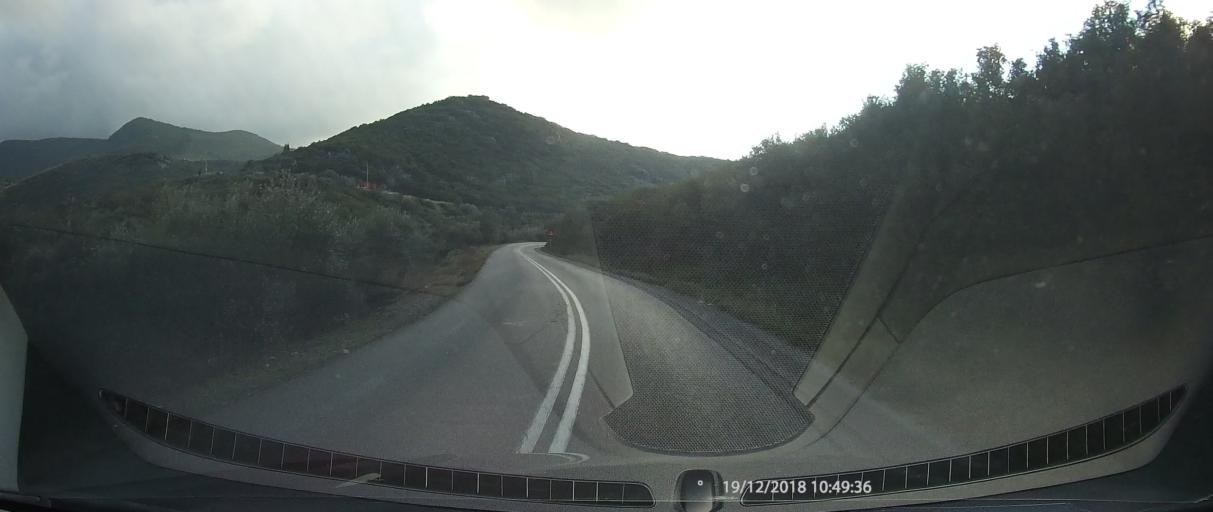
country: GR
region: Peloponnese
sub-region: Nomos Messinias
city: Kardamyli
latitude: 36.9253
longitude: 22.2007
